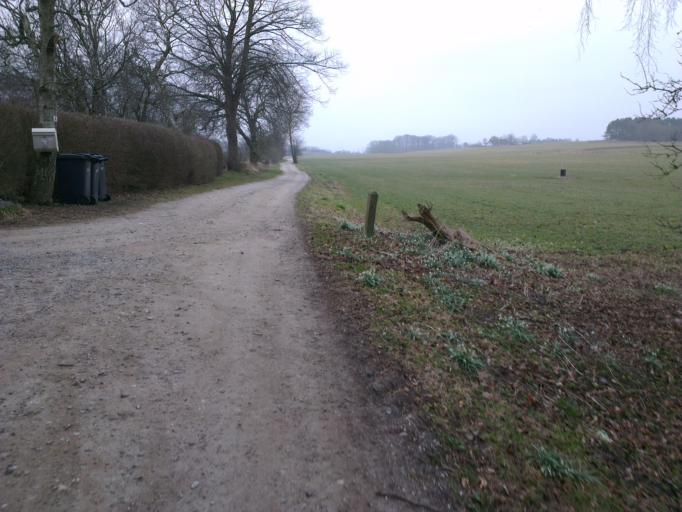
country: DK
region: Capital Region
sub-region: Frederikssund Kommune
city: Frederikssund
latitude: 55.7723
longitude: 12.0360
